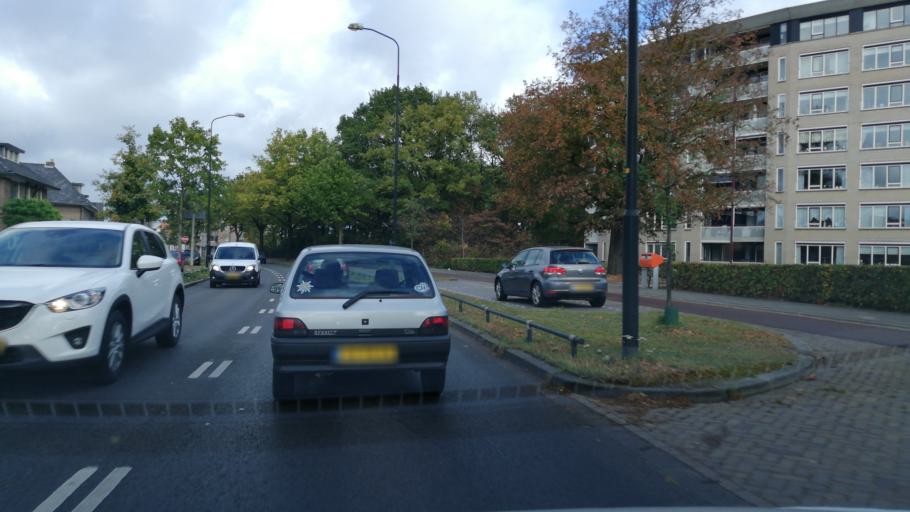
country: NL
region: Gelderland
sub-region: Gemeente Apeldoorn
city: Apeldoorn
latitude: 52.1961
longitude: 5.9622
